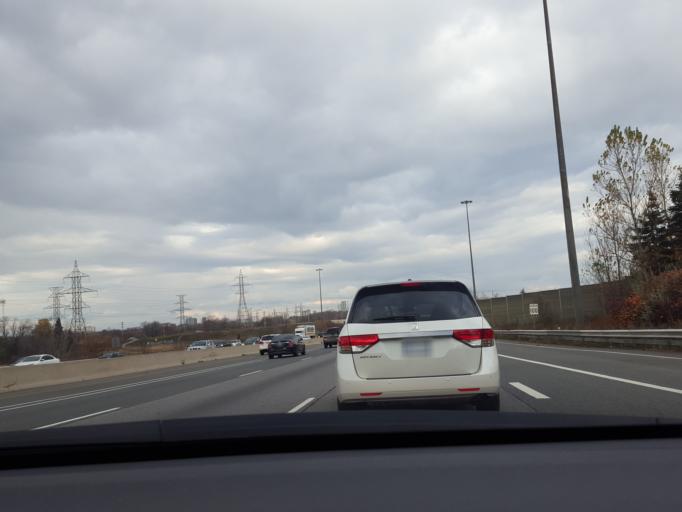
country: CA
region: Ontario
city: Mississauga
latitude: 43.5582
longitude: -79.6898
